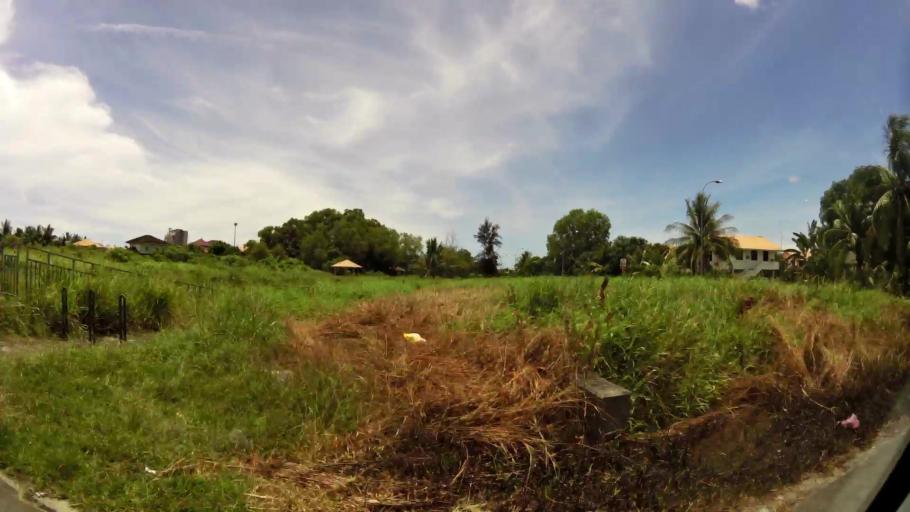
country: BN
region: Belait
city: Kuala Belait
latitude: 4.5895
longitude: 114.2448
